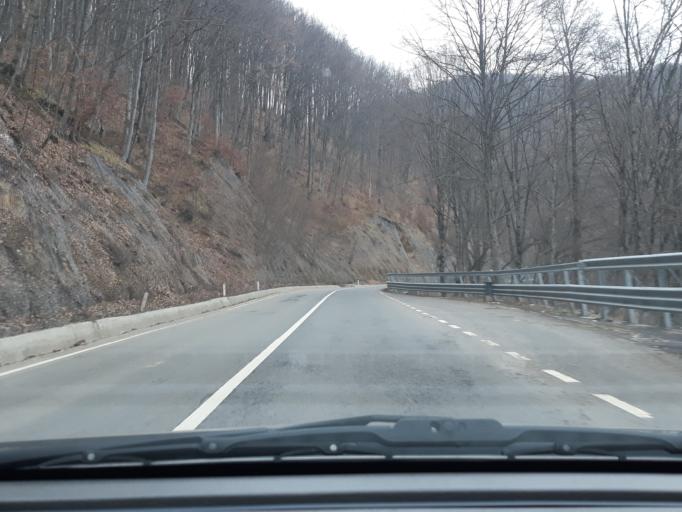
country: RO
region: Bihor
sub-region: Oras Alesd
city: Pestis
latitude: 47.1069
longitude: 22.4053
